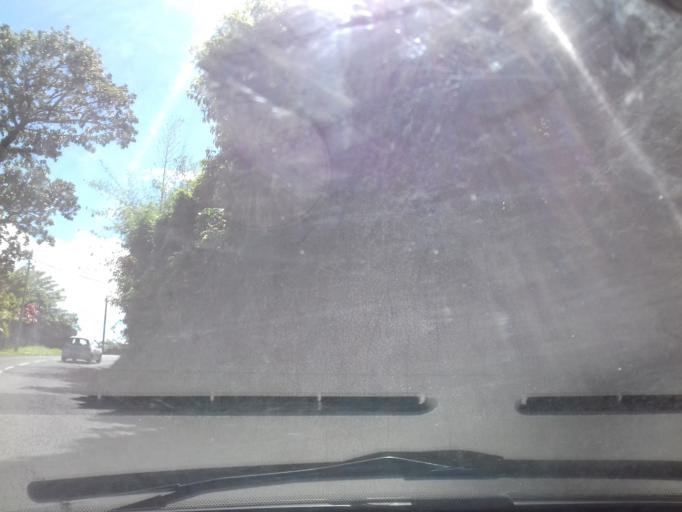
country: MQ
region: Martinique
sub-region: Martinique
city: Saint-Joseph
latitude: 14.6428
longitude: -61.0534
